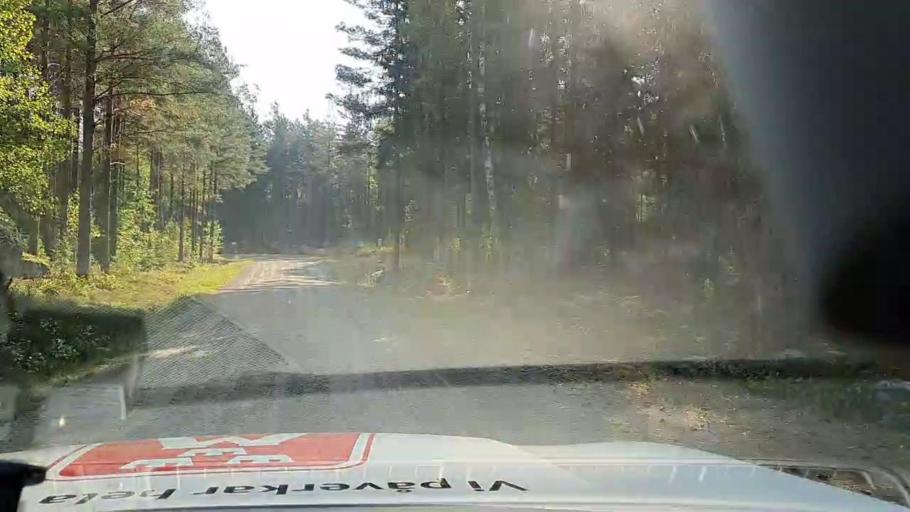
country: SE
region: Soedermanland
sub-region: Eskilstuna Kommun
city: Kvicksund
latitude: 59.3313
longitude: 16.2241
